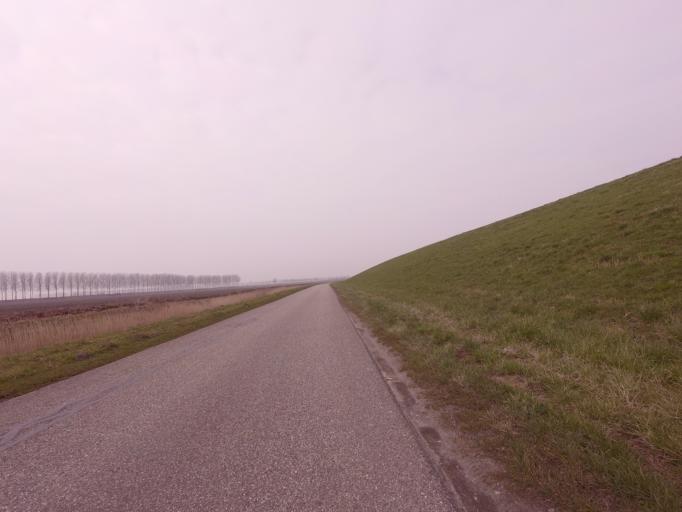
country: NL
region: Zeeland
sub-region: Gemeente Hulst
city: Hulst
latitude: 51.3362
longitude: 4.1313
